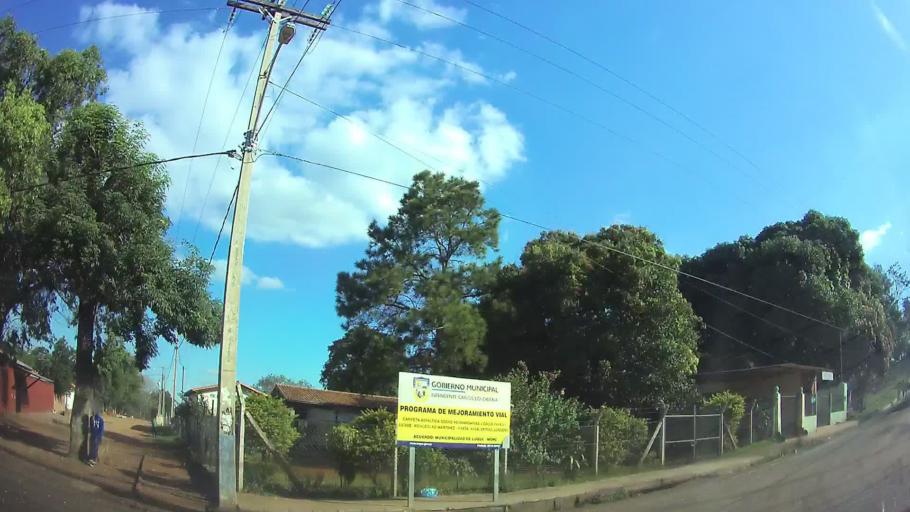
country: PY
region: Central
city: Aregua
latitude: -25.2763
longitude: -57.4453
